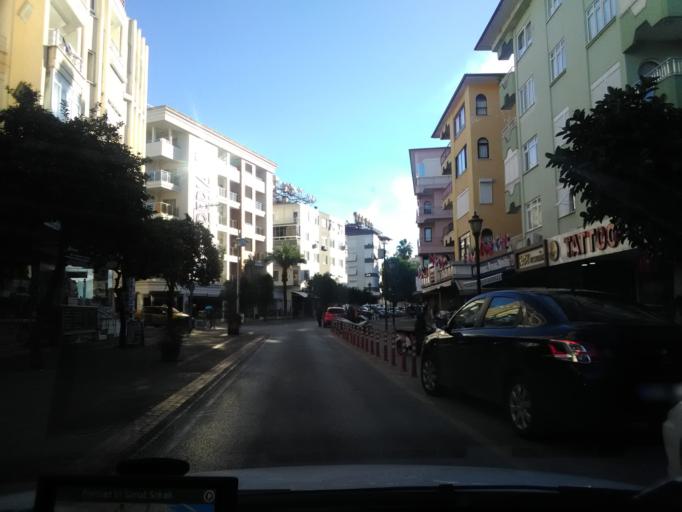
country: TR
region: Antalya
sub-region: Alanya
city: Alanya
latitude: 36.5437
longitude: 31.9895
